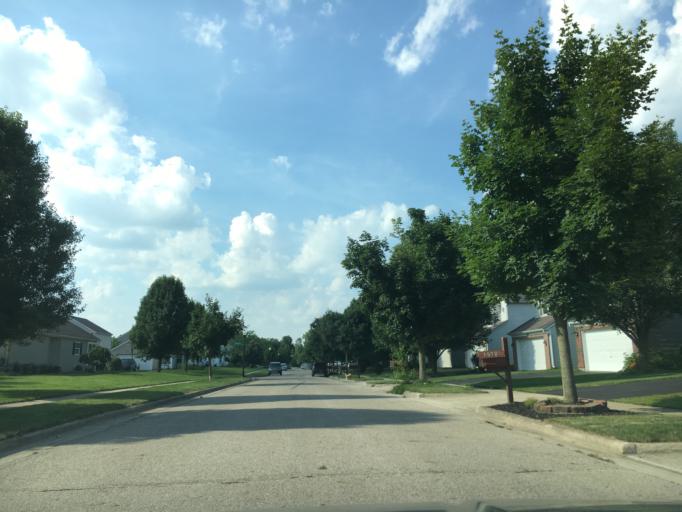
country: US
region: Ohio
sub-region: Franklin County
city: Hilliard
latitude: 39.9896
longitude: -83.1619
